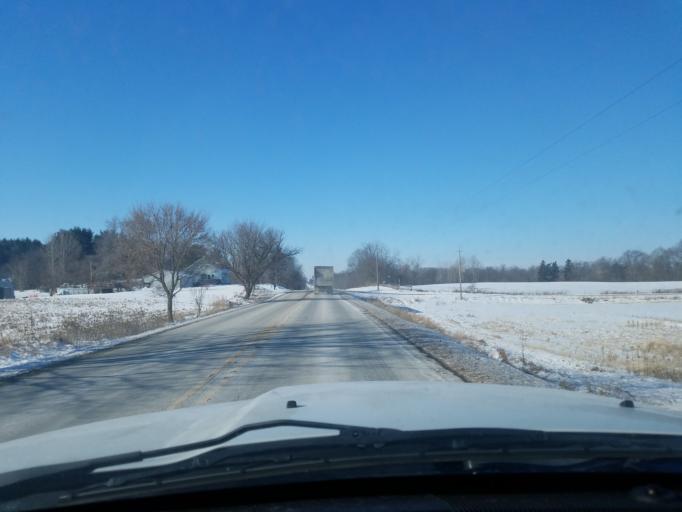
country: US
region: Indiana
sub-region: Noble County
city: Albion
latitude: 41.3958
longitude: -85.3565
